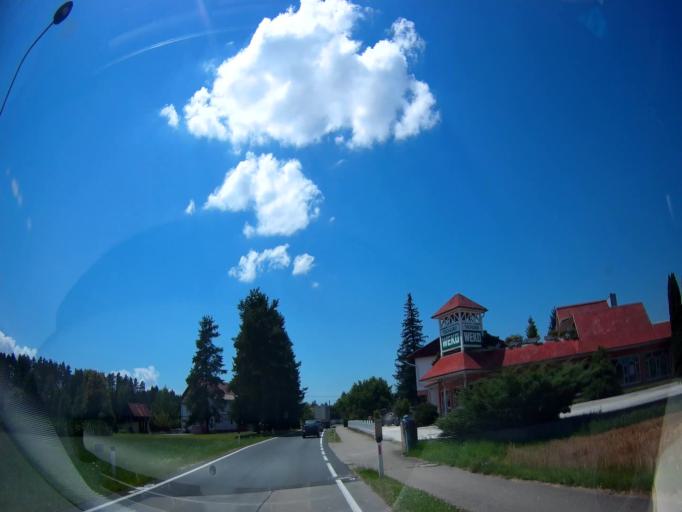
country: AT
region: Carinthia
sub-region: Politischer Bezirk Volkermarkt
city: Globasnitz
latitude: 46.6050
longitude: 14.7153
